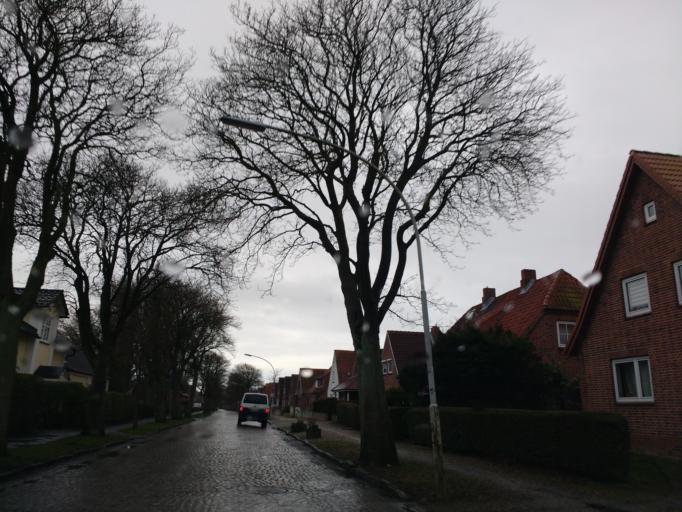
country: DE
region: Schleswig-Holstein
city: Burg auf Fehmarn
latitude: 54.4302
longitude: 11.1952
